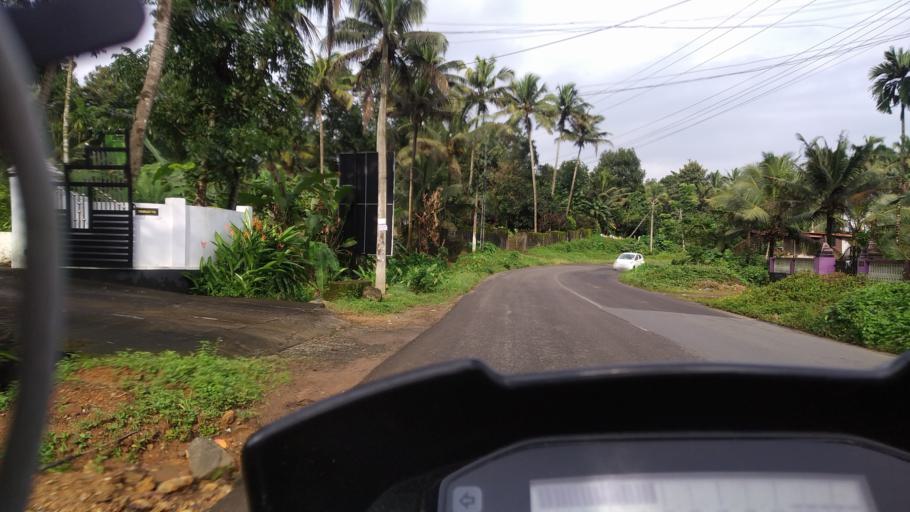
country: IN
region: Kerala
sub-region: Ernakulam
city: Kotamangalam
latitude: 10.0522
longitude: 76.7050
